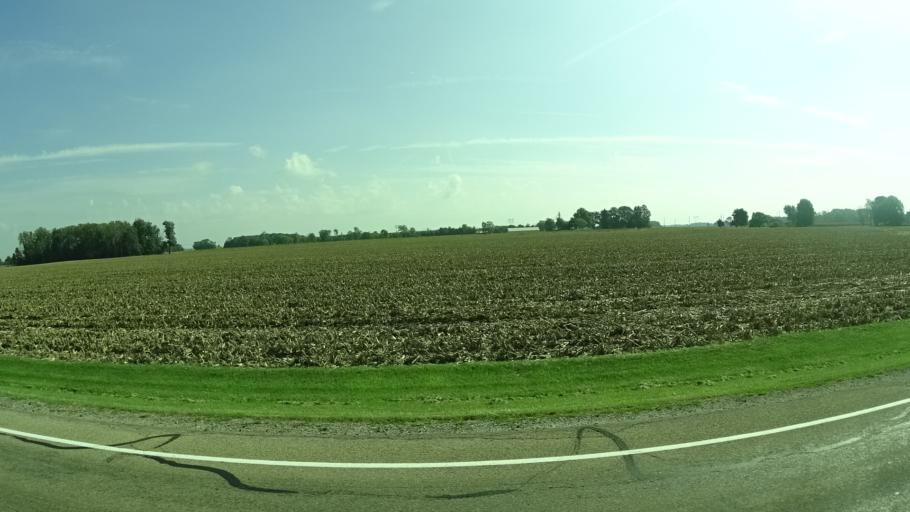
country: US
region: Indiana
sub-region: Madison County
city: Ingalls
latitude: 40.0041
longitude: -85.8432
